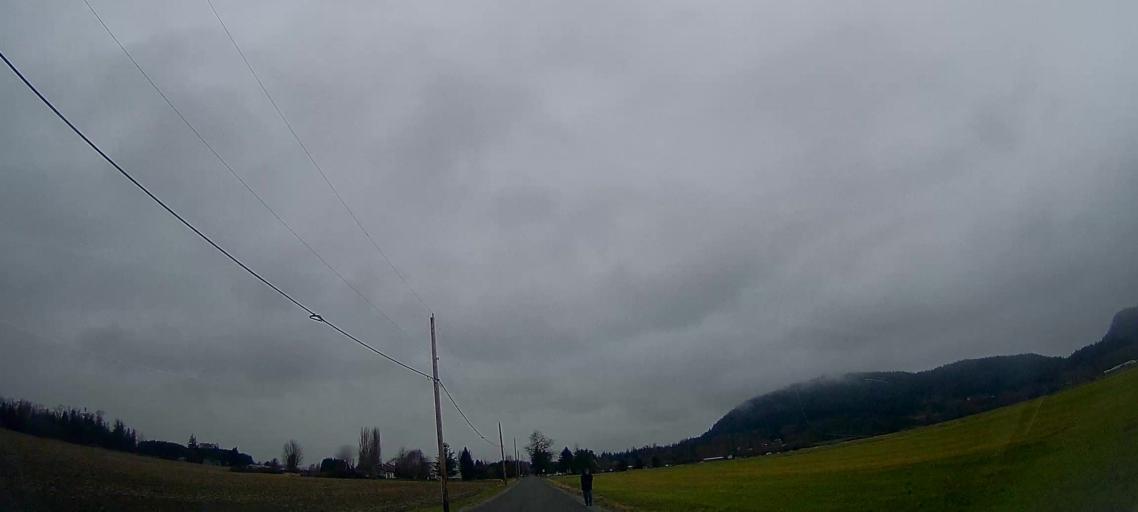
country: US
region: Washington
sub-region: Skagit County
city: Mount Vernon
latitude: 48.3717
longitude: -122.3240
